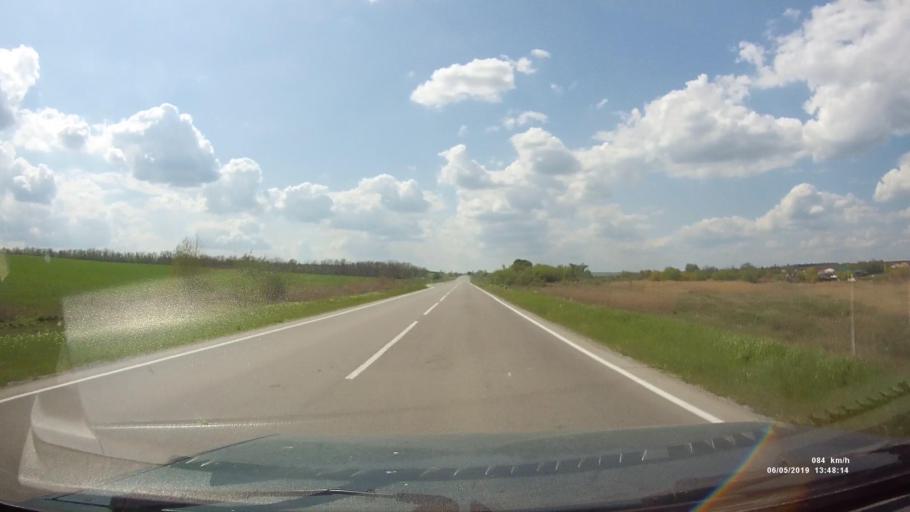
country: RU
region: Rostov
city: Melikhovskaya
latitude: 47.6580
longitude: 40.5473
